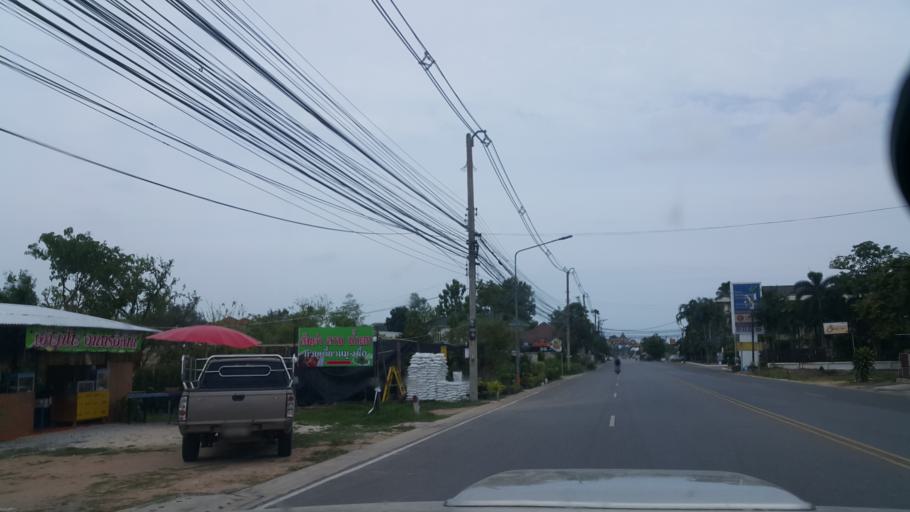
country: TH
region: Rayong
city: Ban Chang
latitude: 12.7152
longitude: 101.0493
